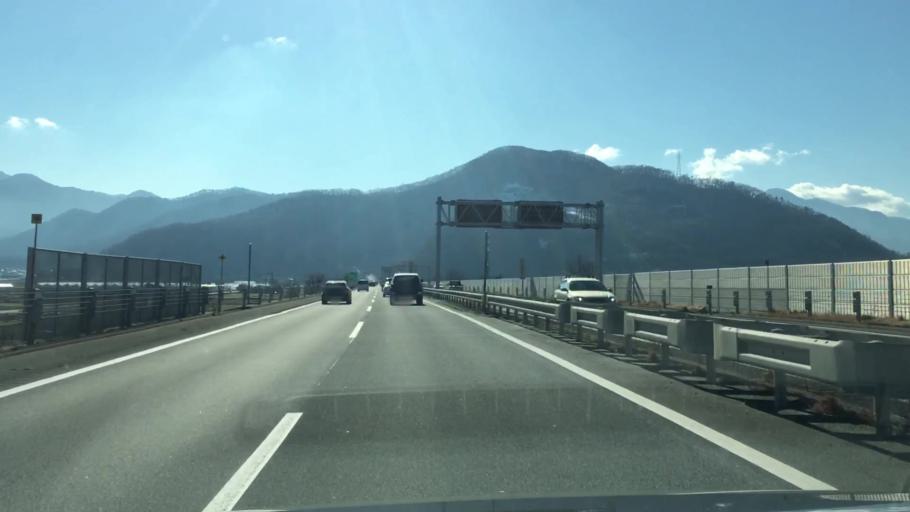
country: JP
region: Nagano
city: Nagano-shi
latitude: 36.5445
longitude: 138.1392
